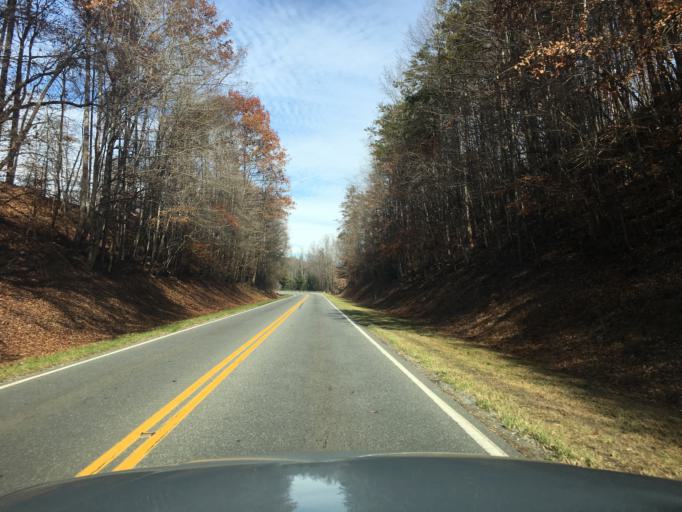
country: US
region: North Carolina
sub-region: McDowell County
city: Marion
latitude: 35.6554
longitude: -81.9748
